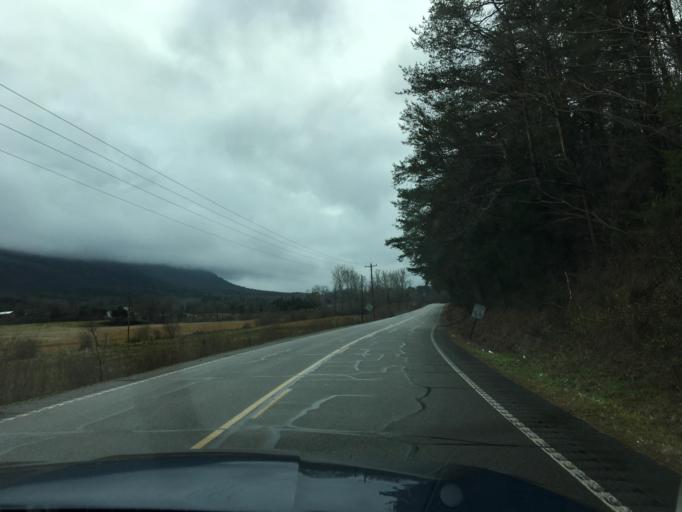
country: US
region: Tennessee
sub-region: Polk County
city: Benton
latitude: 35.1633
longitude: -84.6344
